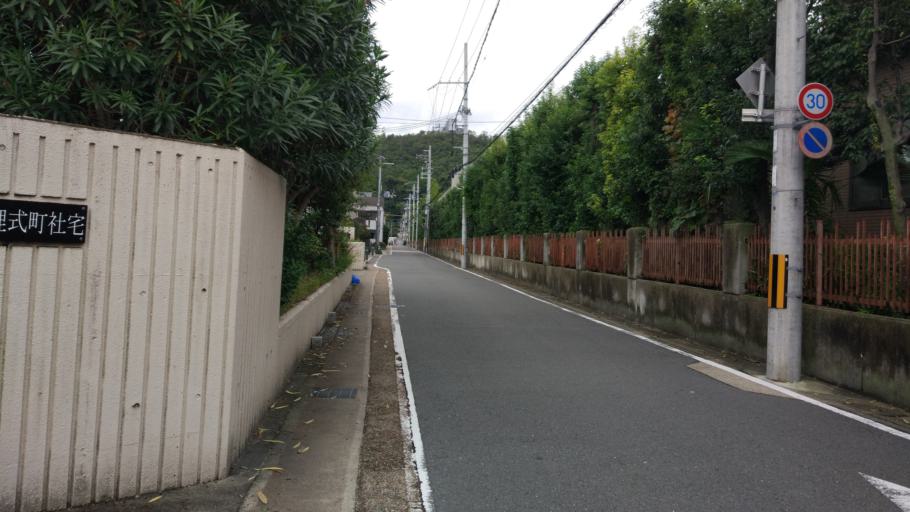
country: JP
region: Kyoto
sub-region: Kyoto-shi
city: Kamigyo-ku
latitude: 35.0487
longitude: 135.7793
